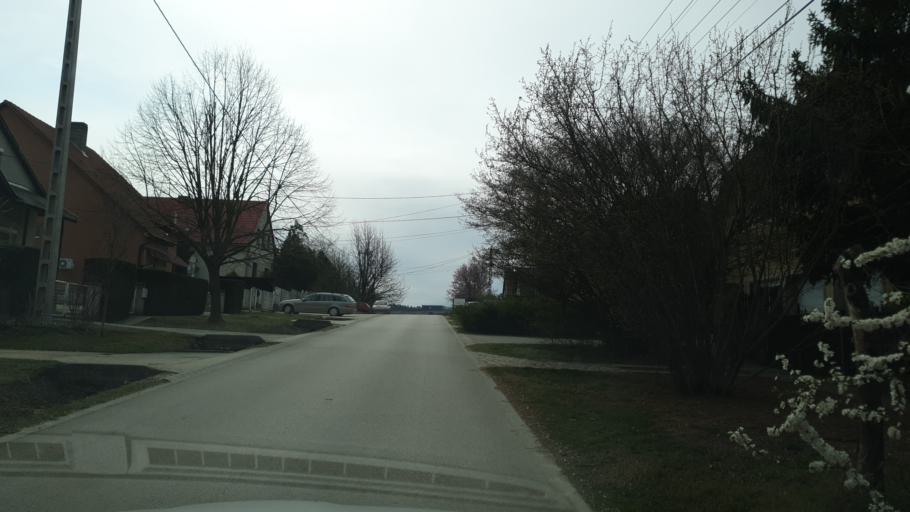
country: HU
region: Fejer
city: Etyek
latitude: 47.4521
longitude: 18.7495
